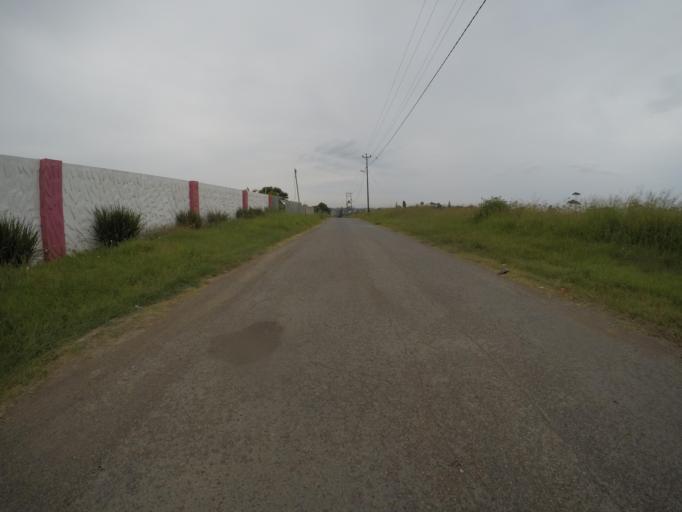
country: ZA
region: Eastern Cape
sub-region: Buffalo City Metropolitan Municipality
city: East London
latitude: -33.0062
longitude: 27.8527
